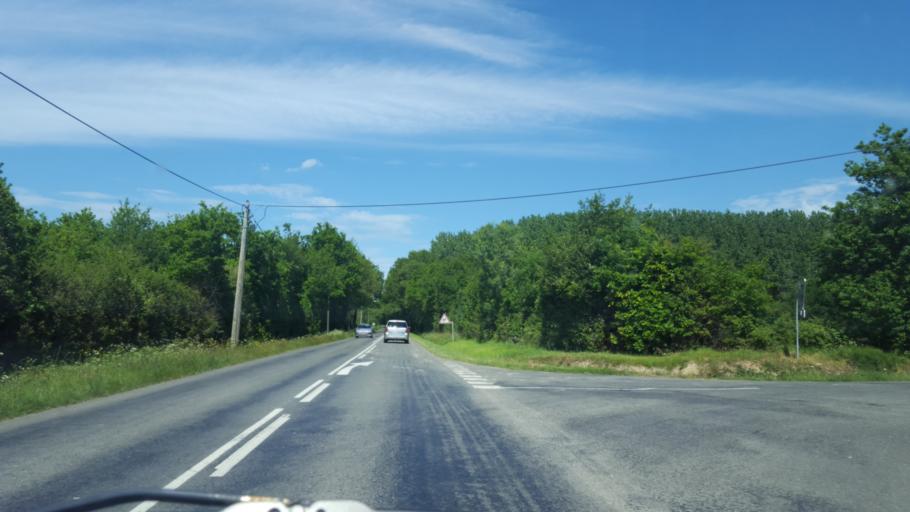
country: FR
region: Pays de la Loire
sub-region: Departement de la Loire-Atlantique
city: Saint-Philbert-de-Grand-Lieu
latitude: 47.0043
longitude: -1.6610
